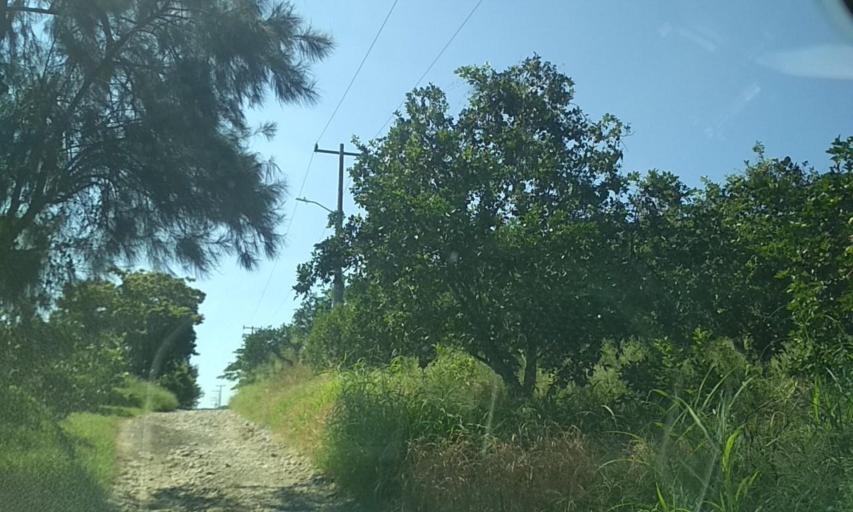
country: MX
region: Veracruz
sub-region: Martinez de la Torre
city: La Union Paso Largo
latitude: 20.1520
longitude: -96.9974
